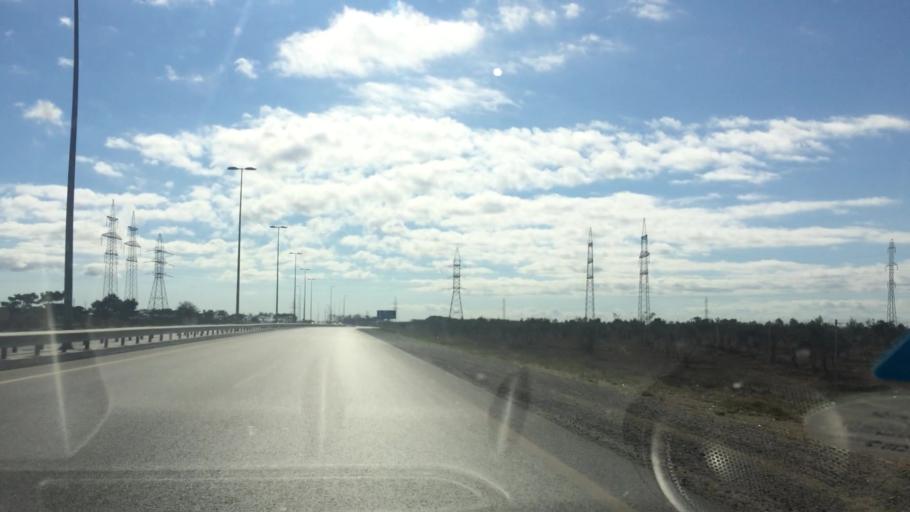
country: AZ
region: Baki
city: Qala
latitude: 40.4390
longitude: 50.1825
